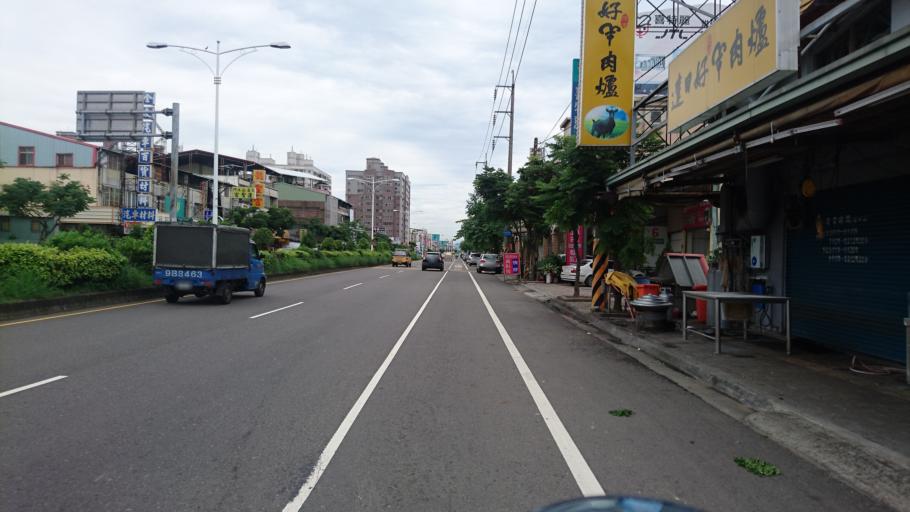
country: TW
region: Taiwan
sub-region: Taichung City
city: Taichung
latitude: 24.0685
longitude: 120.6963
